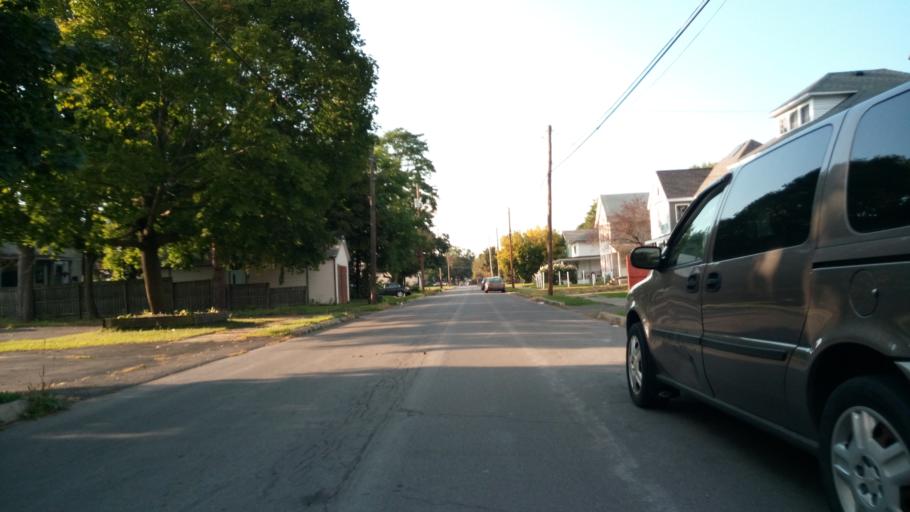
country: US
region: New York
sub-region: Chemung County
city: Elmira
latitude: 42.1067
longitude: -76.8046
